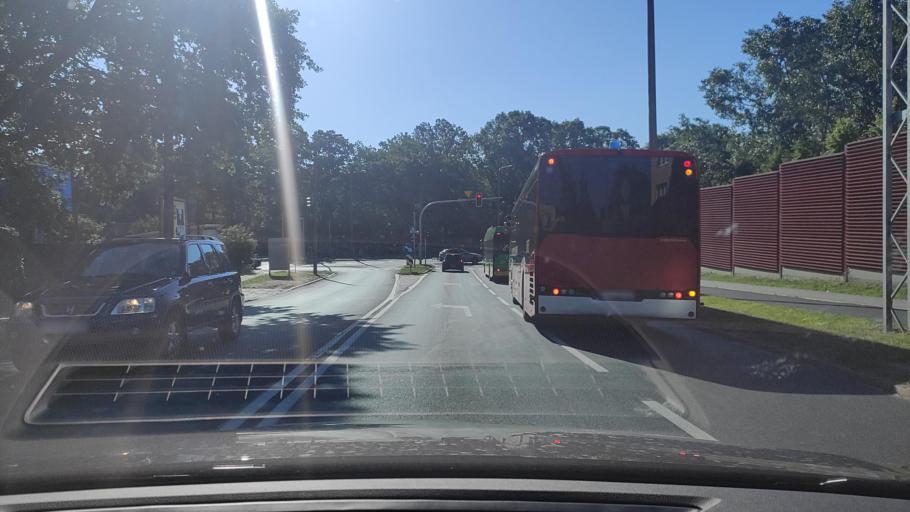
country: PL
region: Greater Poland Voivodeship
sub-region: Powiat poznanski
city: Lubon
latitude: 52.3696
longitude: 16.9139
